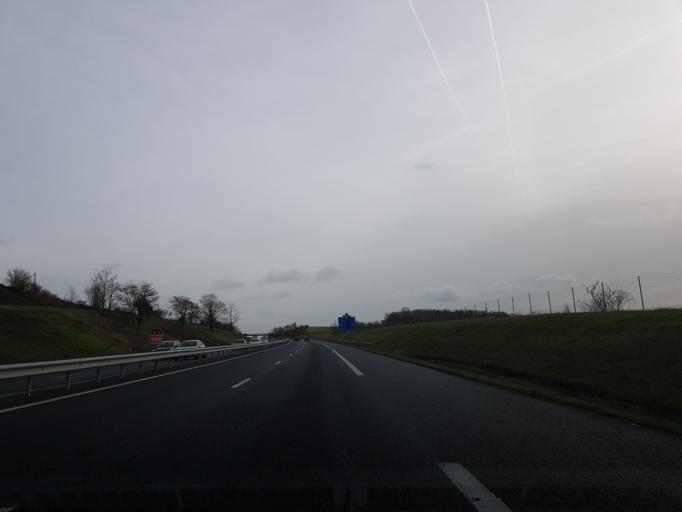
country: FR
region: Bourgogne
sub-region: Departement de l'Yonne
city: Soucy
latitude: 48.2628
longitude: 3.3088
